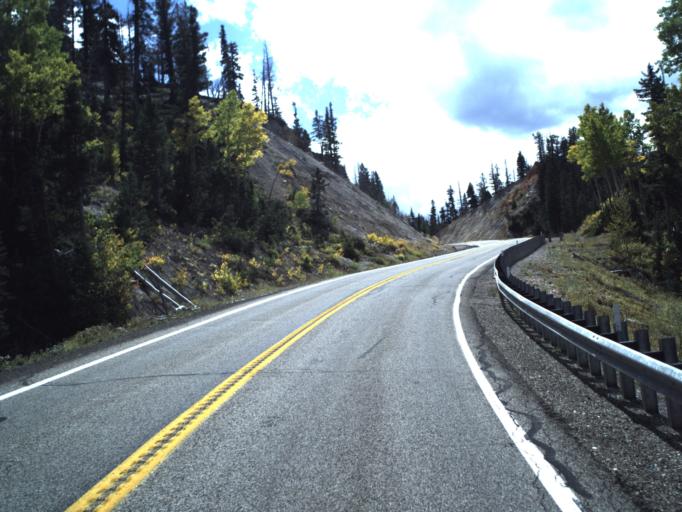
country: US
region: Utah
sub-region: Iron County
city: Cedar City
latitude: 37.5892
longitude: -112.8816
